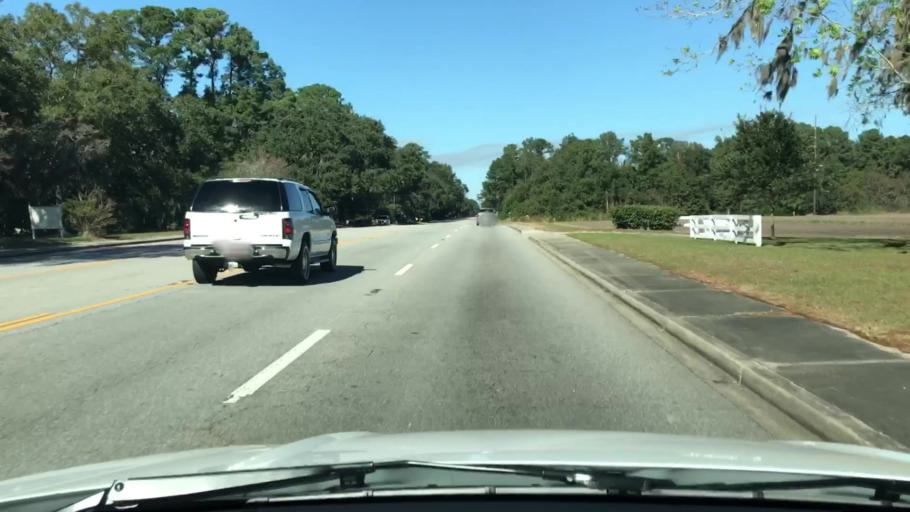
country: US
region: South Carolina
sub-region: Beaufort County
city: Laurel Bay
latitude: 32.5507
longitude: -80.7440
